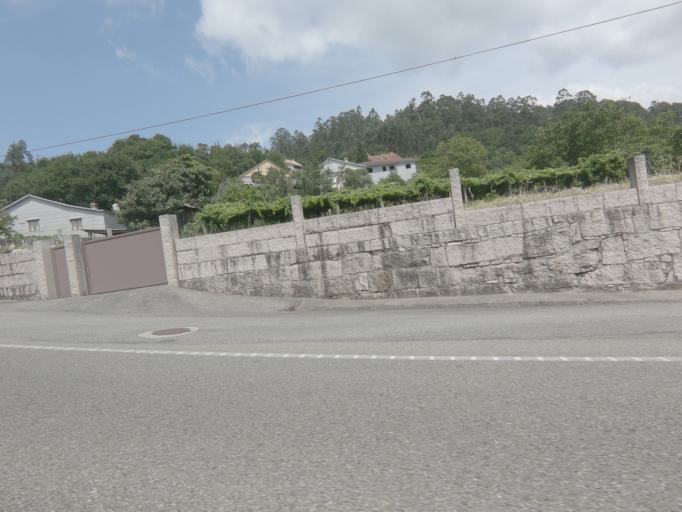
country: ES
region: Galicia
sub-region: Provincia de Pontevedra
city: Tomino
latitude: 42.0417
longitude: -8.7287
